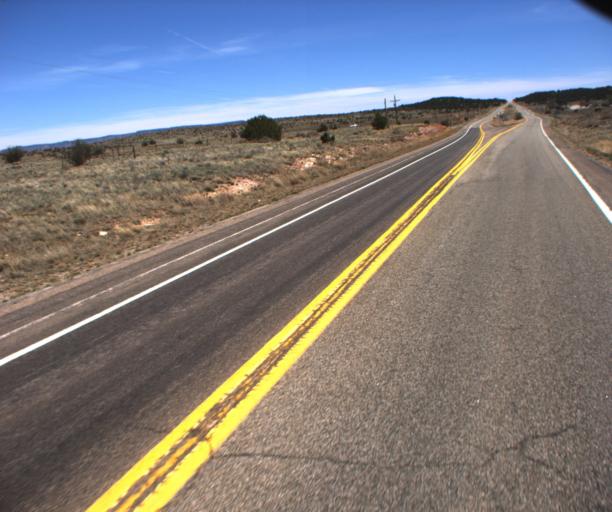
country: US
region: Arizona
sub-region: Mohave County
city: Peach Springs
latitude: 35.5323
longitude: -113.2395
